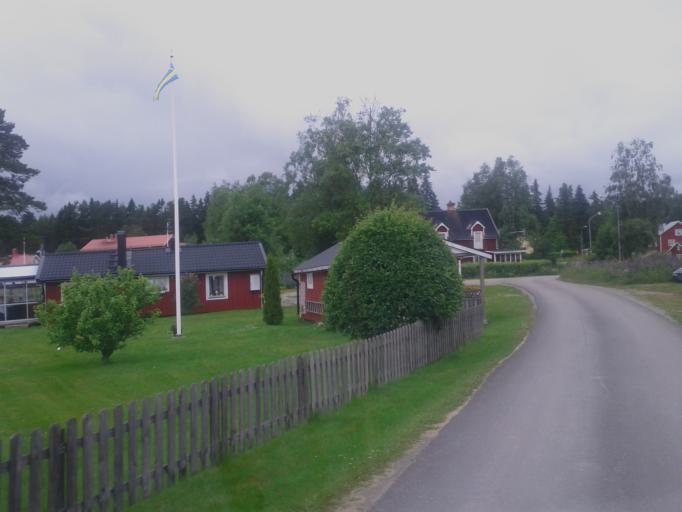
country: SE
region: Gaevleborg
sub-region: Nordanstigs Kommun
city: Bergsjoe
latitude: 61.9571
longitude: 17.3380
